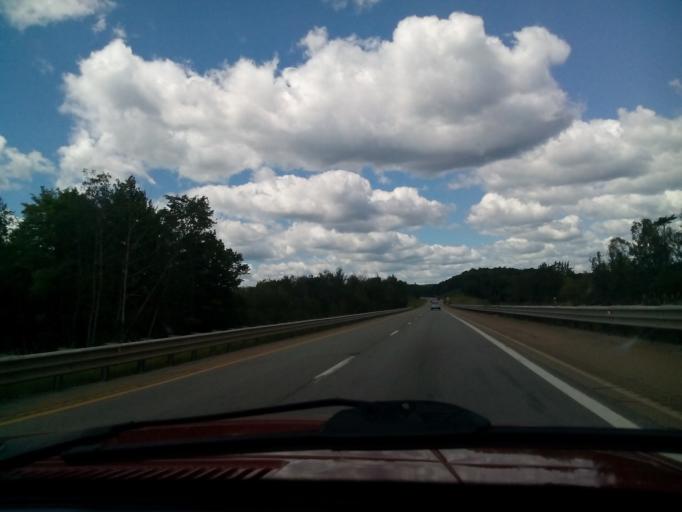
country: US
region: Michigan
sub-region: Ogemaw County
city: West Branch
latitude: 44.2766
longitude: -84.2818
